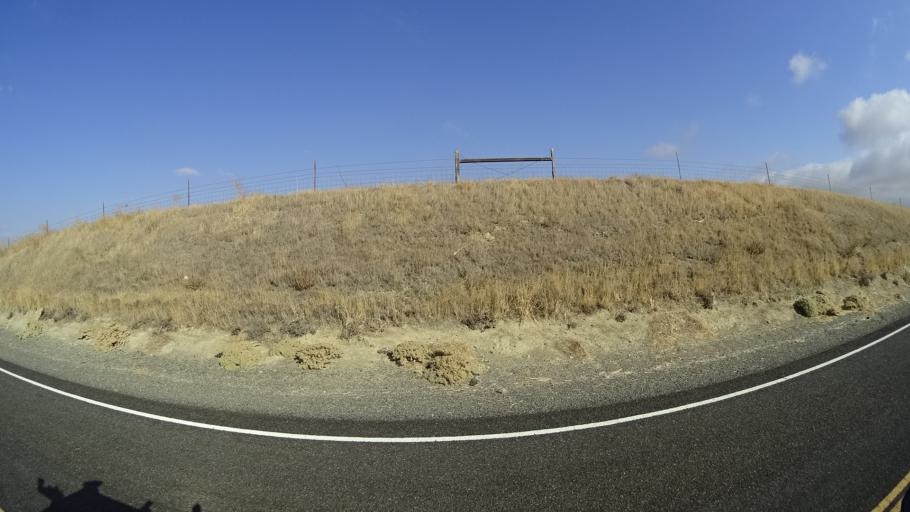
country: US
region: California
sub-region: Yolo County
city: Esparto
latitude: 38.7806
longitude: -121.9821
